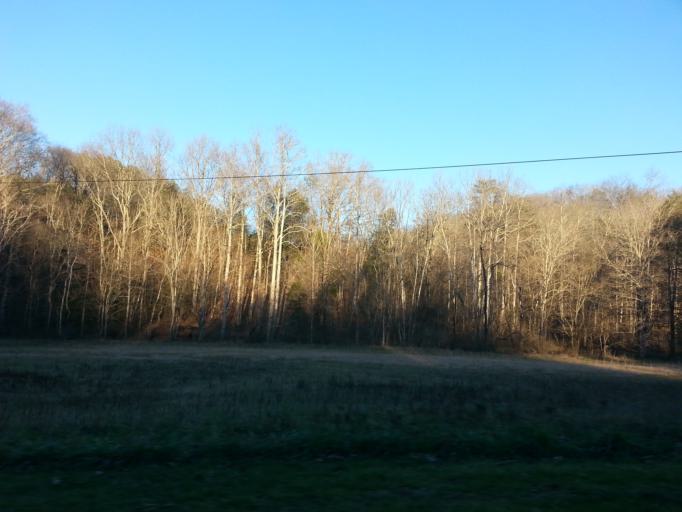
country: US
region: Tennessee
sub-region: Knox County
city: Knoxville
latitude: 35.9251
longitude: -83.8269
